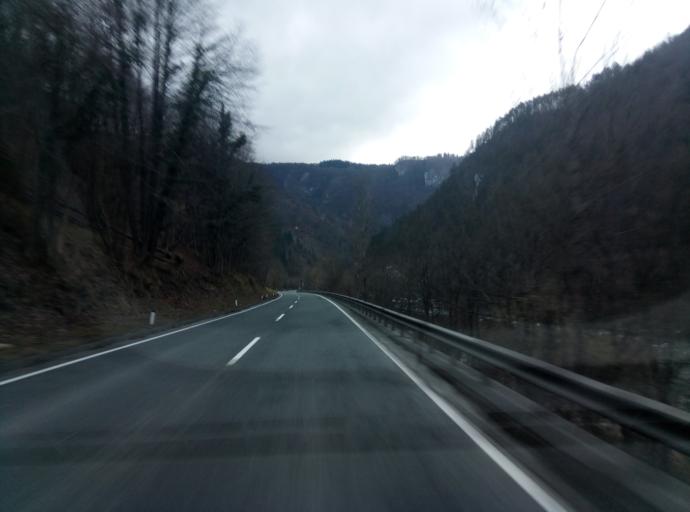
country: SI
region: Zagorje ob Savi
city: Zagorje ob Savi
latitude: 46.1137
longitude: 15.0164
